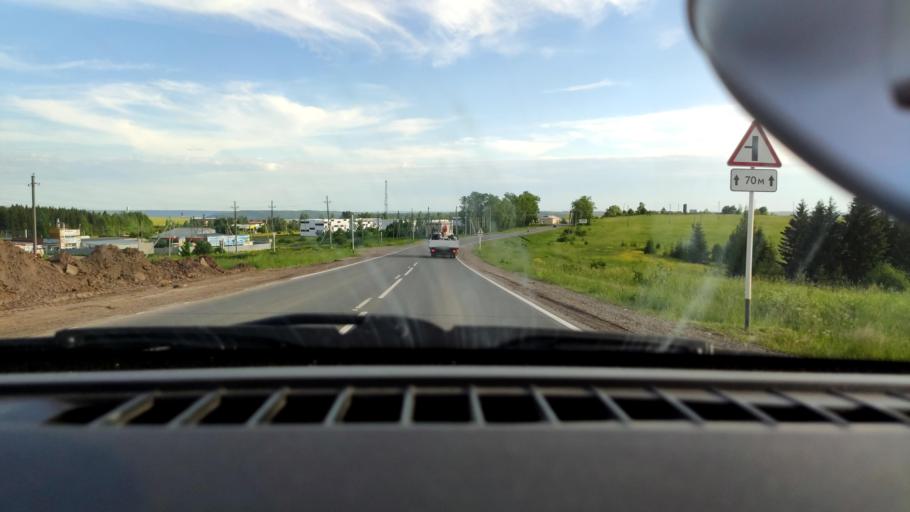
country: RU
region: Perm
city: Nytva
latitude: 57.9564
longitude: 55.3582
